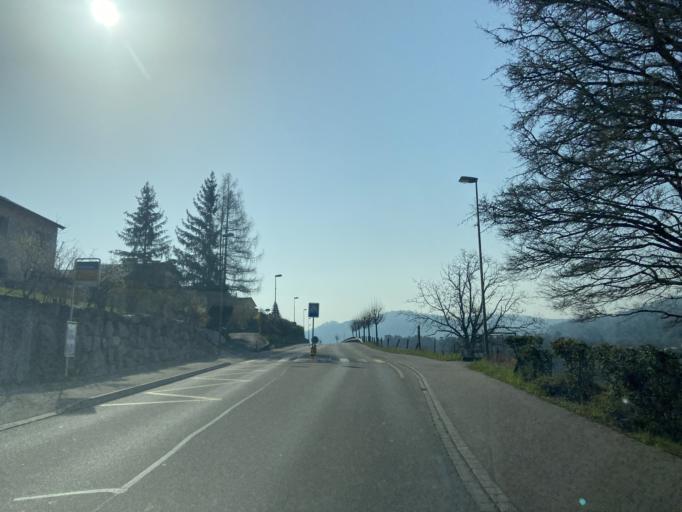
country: CH
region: Zurich
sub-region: Bezirk Winterthur
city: Neftenbach / Dorf Neftenbach
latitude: 47.5217
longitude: 8.6705
